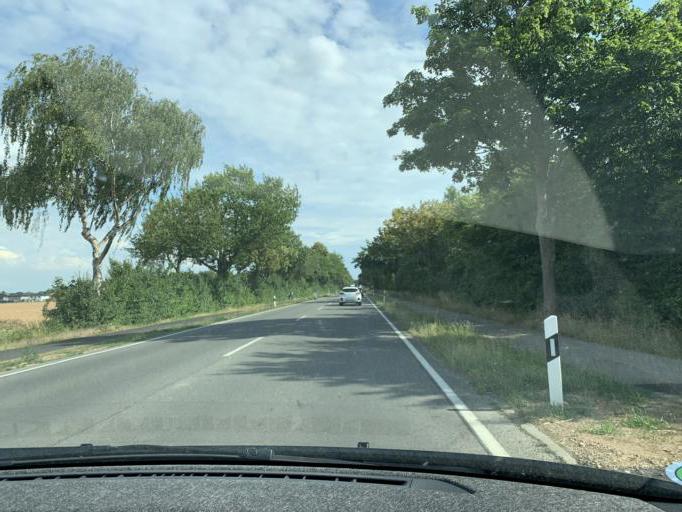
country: DE
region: North Rhine-Westphalia
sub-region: Regierungsbezirk Koln
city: Niederzier
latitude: 50.8589
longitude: 6.4382
